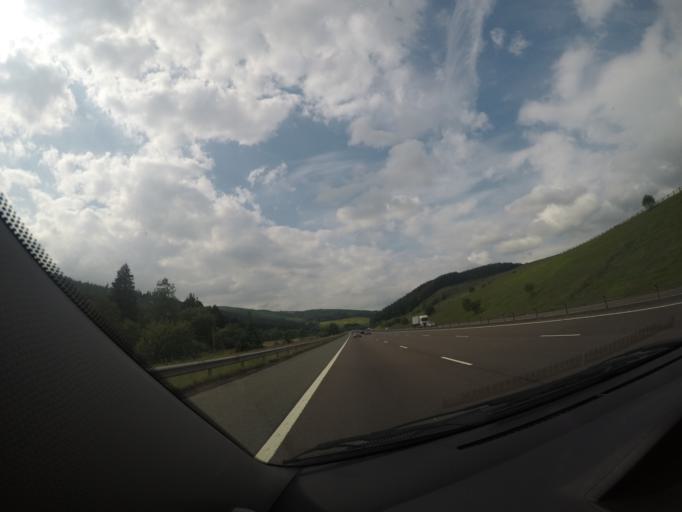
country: GB
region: Scotland
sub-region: Dumfries and Galloway
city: Moffat
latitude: 55.3544
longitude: -3.5096
